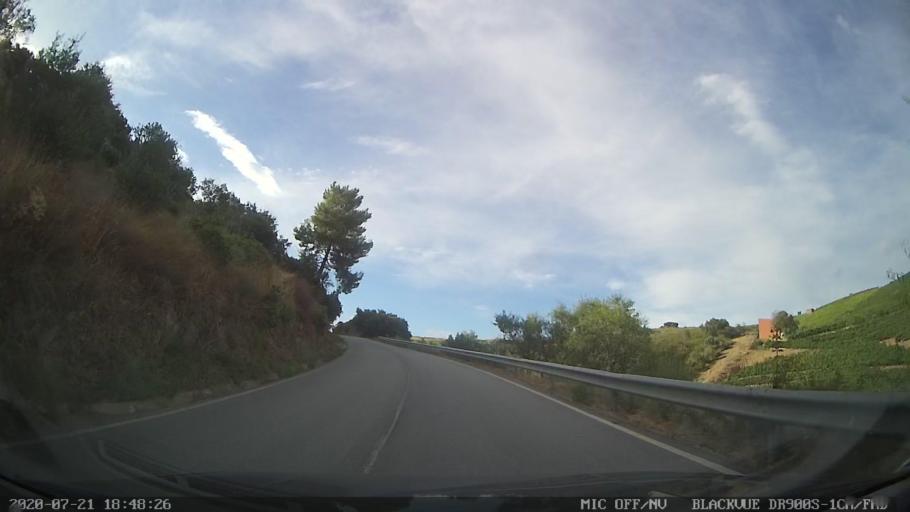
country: PT
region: Viseu
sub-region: Sao Joao da Pesqueira
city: Sao Joao da Pesqueira
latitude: 41.1281
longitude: -7.4360
